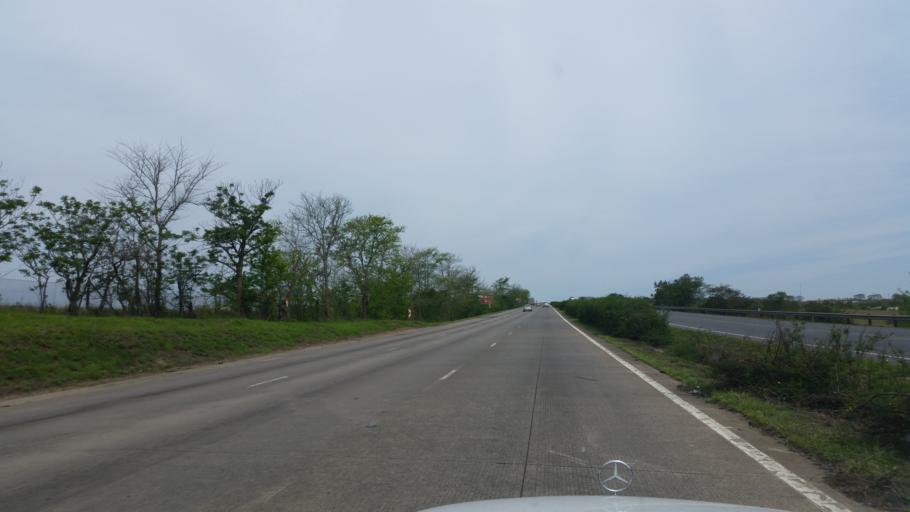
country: ZA
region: KwaZulu-Natal
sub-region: uMgungundlovu District Municipality
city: Camperdown
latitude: -29.6818
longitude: 30.4739
